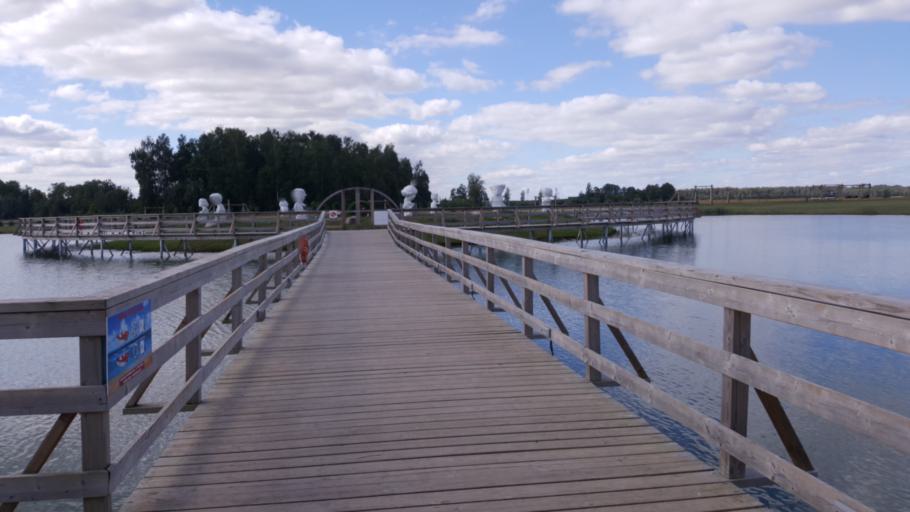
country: LT
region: Siauliu apskritis
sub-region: Siauliai
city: Siauliai
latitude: 56.0203
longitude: 23.4991
